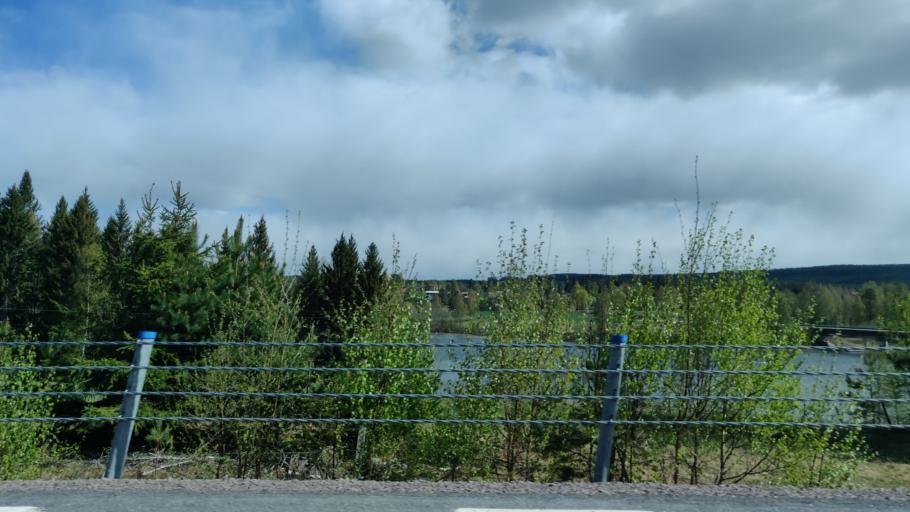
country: SE
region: Vaermland
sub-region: Hagfors Kommun
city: Hagfors
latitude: 59.8811
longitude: 13.7045
